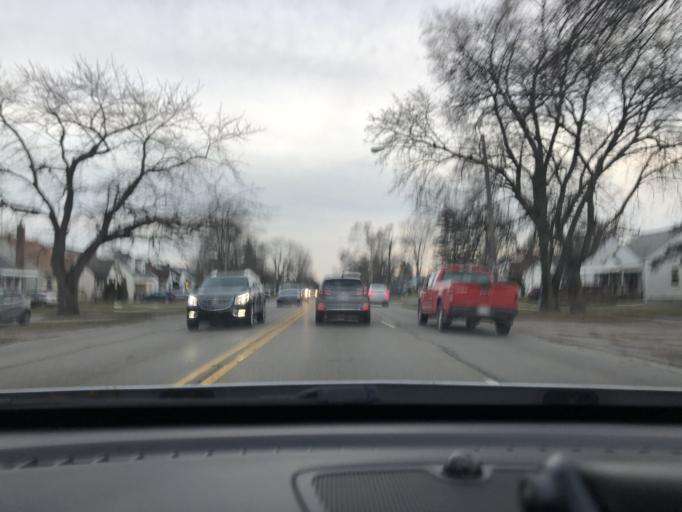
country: US
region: Michigan
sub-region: Wayne County
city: Allen Park
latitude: 42.2607
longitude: -83.2315
